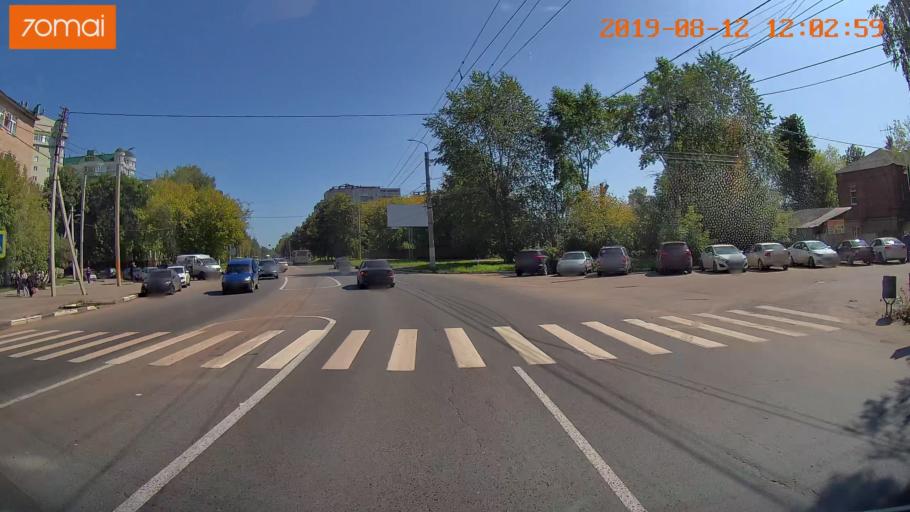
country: RU
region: Ivanovo
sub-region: Gorod Ivanovo
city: Ivanovo
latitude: 56.9948
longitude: 40.9965
